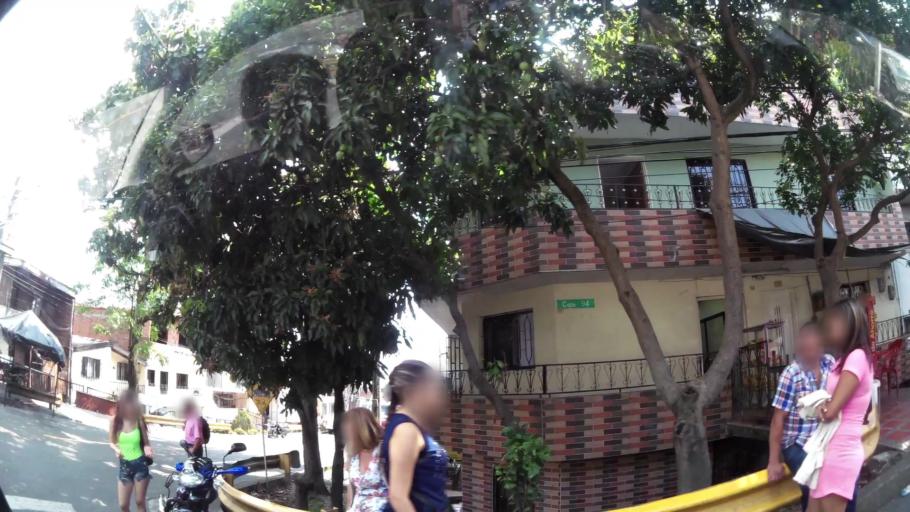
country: CO
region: Antioquia
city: Medellin
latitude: 6.2901
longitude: -75.5772
